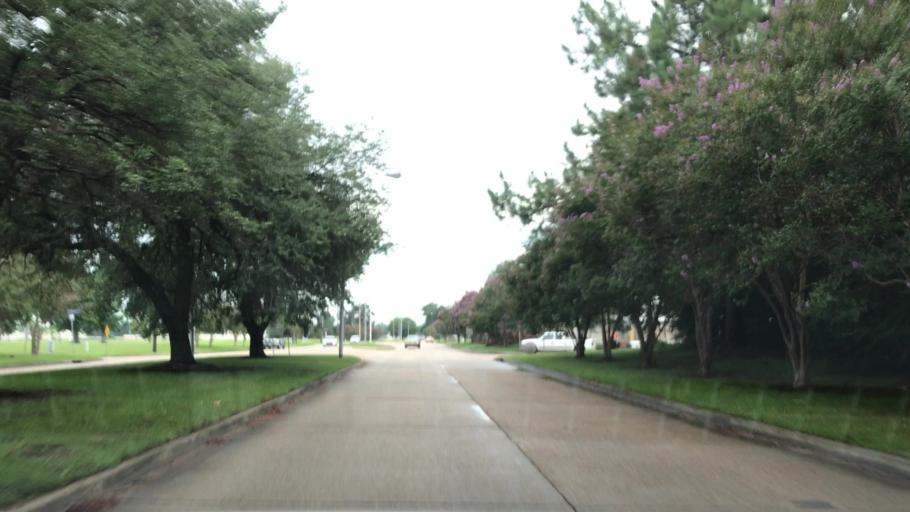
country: US
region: Louisiana
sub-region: East Baton Rouge Parish
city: Brownsfield
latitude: 30.5337
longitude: -91.1614
